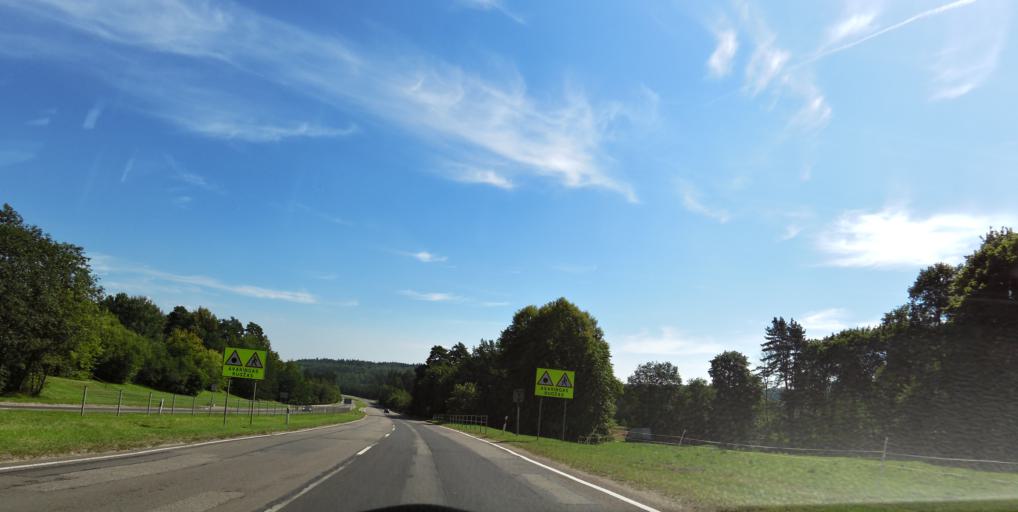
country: LT
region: Vilnius County
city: Rasos
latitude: 54.6918
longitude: 25.3583
